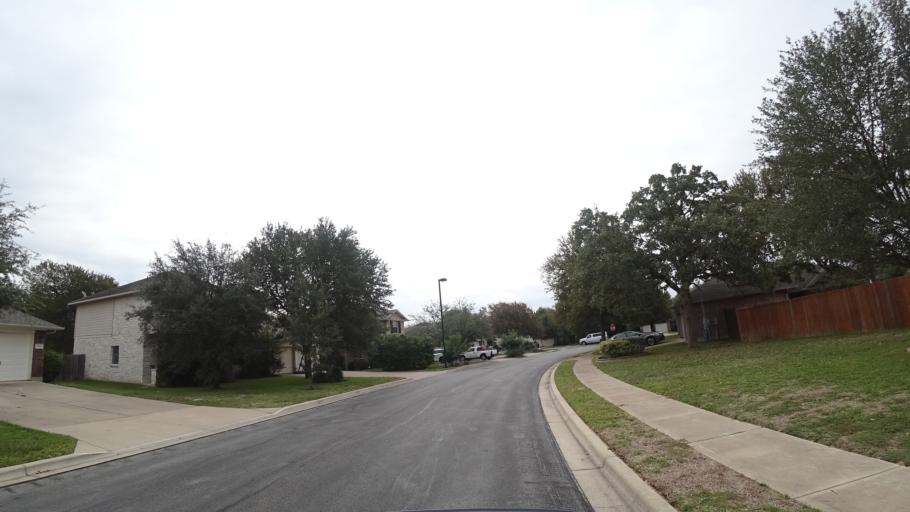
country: US
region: Texas
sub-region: Travis County
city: Shady Hollow
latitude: 30.1950
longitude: -97.9036
